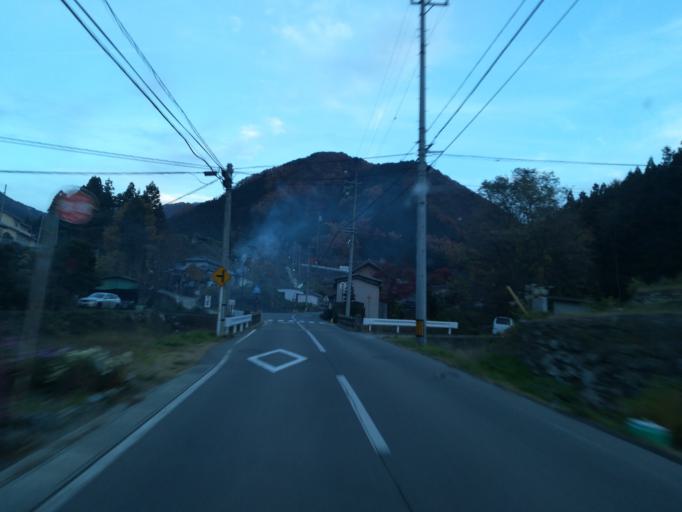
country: JP
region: Nagano
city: Suzaka
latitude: 36.5824
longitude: 138.2770
